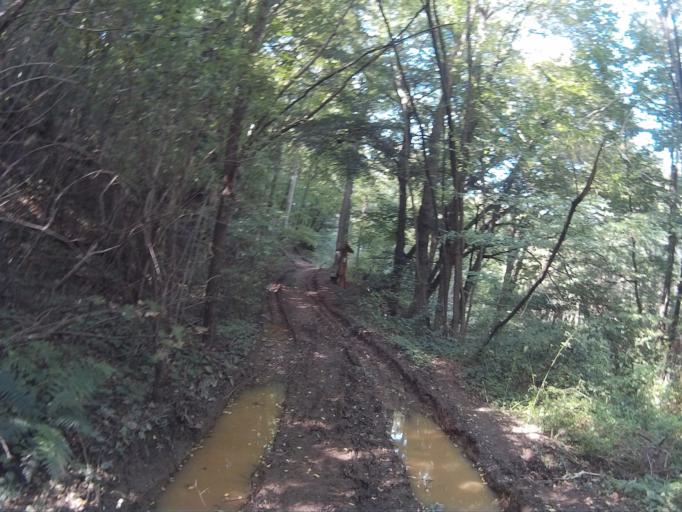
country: HU
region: Vas
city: Koszeg
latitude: 47.4033
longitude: 16.5252
